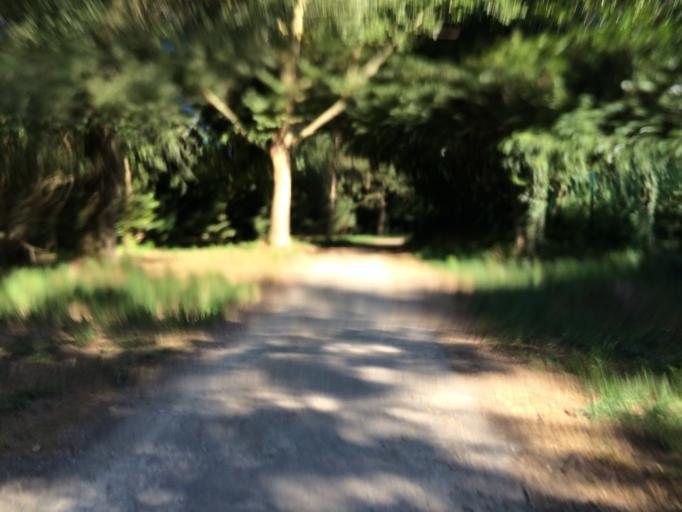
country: FR
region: Ile-de-France
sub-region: Departement de l'Essonne
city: Palaiseau
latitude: 48.7367
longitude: 2.2446
